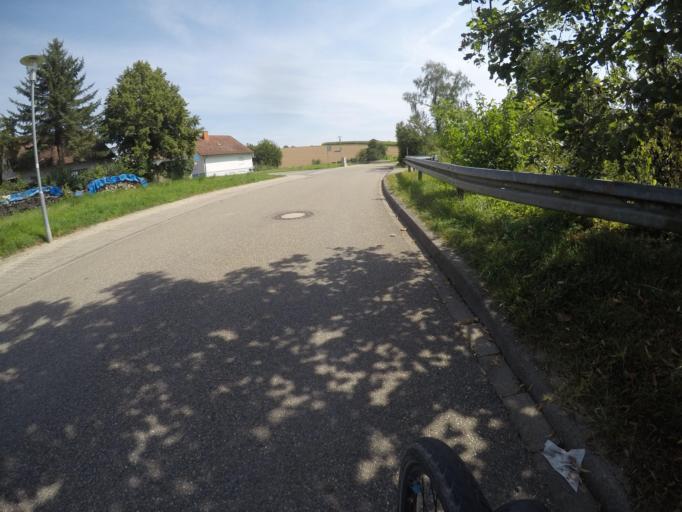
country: DE
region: Baden-Wuerttemberg
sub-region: Karlsruhe Region
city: Gondelsheim
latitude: 49.0579
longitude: 8.6638
